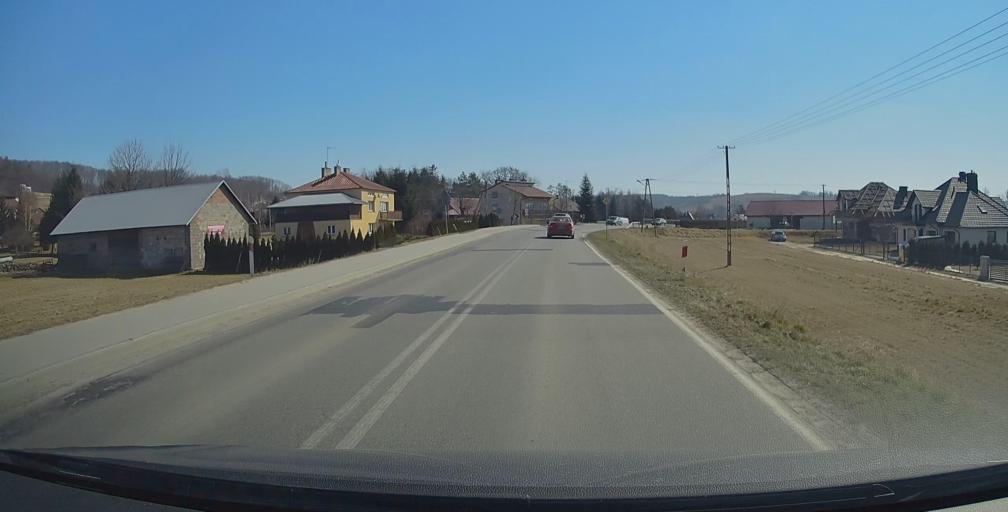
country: PL
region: Subcarpathian Voivodeship
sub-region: Powiat rzeszowski
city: Chmielnik
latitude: 49.9579
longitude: 22.0981
